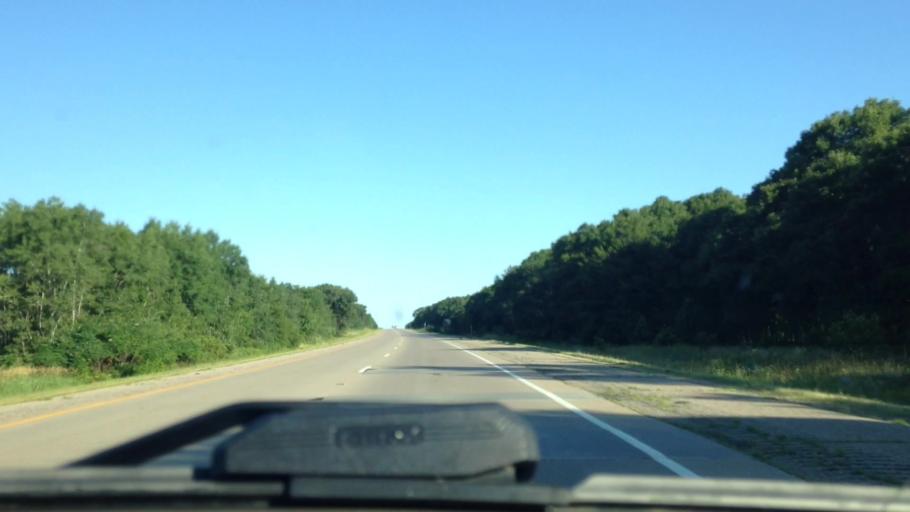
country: US
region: Wisconsin
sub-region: Columbia County
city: Wisconsin Dells
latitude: 43.6923
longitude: -89.8502
